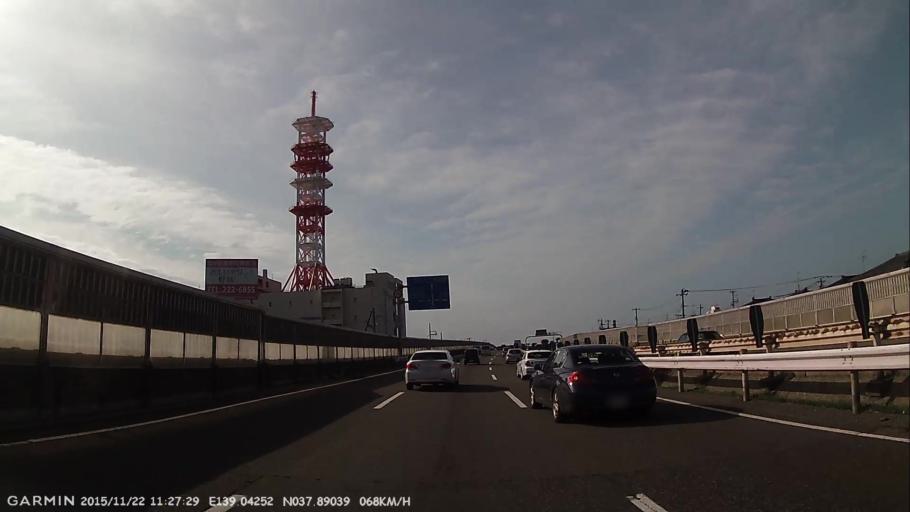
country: JP
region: Niigata
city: Niigata-shi
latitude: 37.8903
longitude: 139.0423
